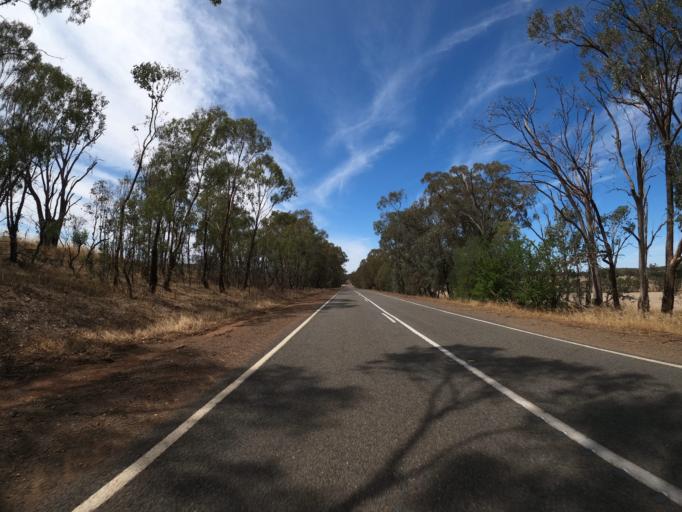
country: AU
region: Victoria
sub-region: Benalla
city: Benalla
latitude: -36.3504
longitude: 145.9627
